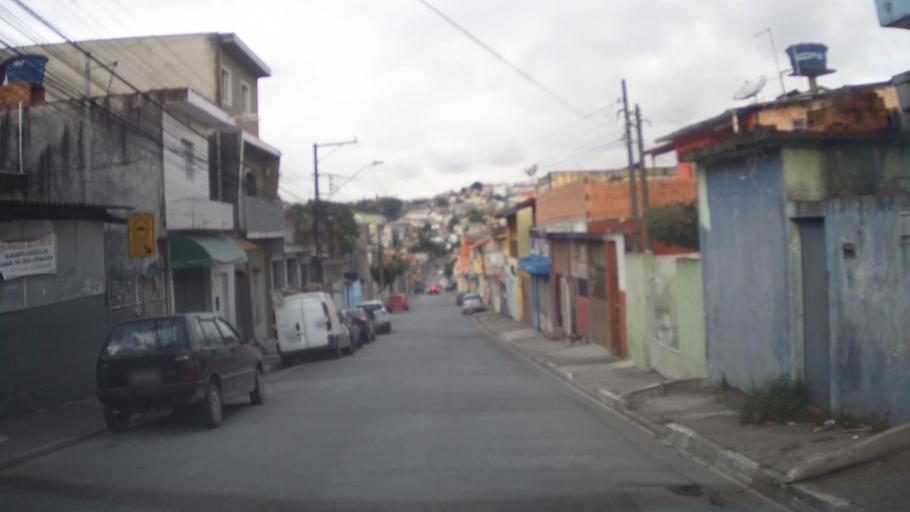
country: BR
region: Sao Paulo
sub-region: Itaquaquecetuba
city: Itaquaquecetuba
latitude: -23.4476
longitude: -46.4223
